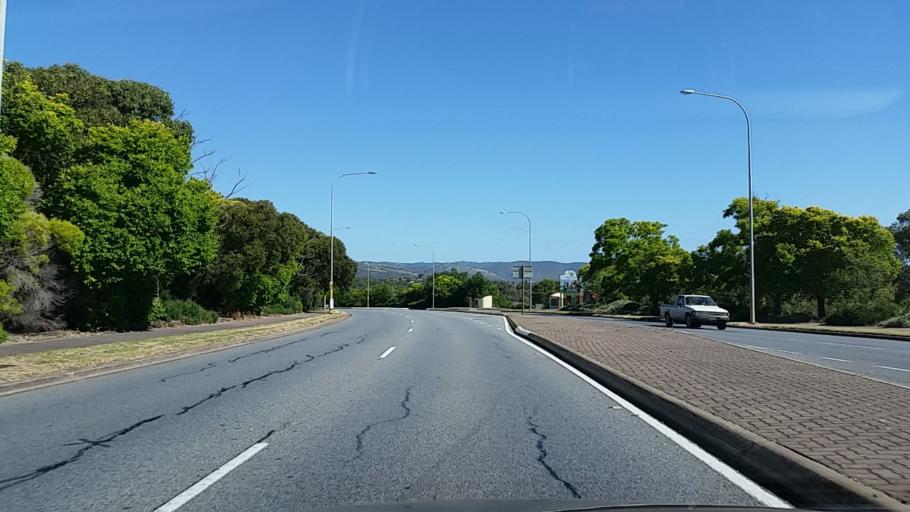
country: AU
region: South Australia
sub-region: Tea Tree Gully
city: Golden Grove
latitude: -34.7932
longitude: 138.6983
